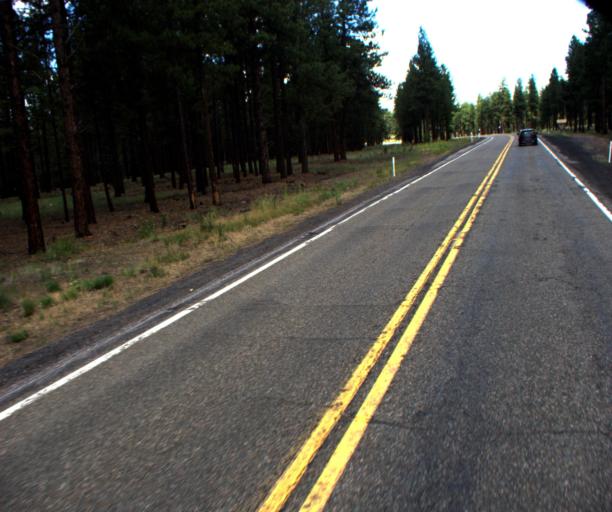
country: US
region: Arizona
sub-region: Coconino County
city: Flagstaff
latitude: 35.2766
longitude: -111.7448
